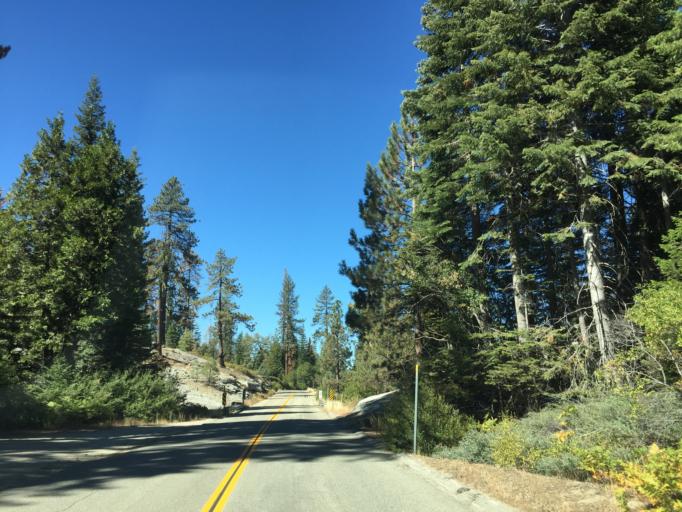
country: US
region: California
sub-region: Fresno County
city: Auberry
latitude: 37.0855
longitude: -119.2145
